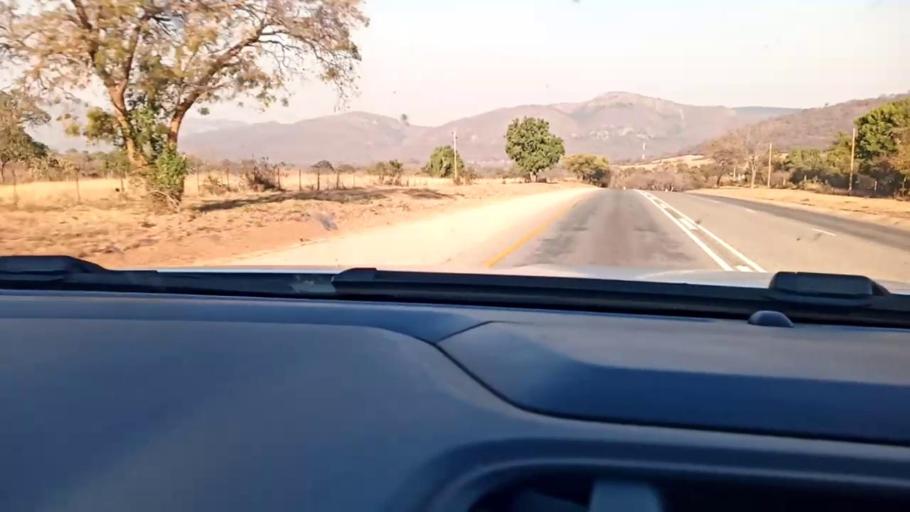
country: ZA
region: Limpopo
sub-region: Mopani District Municipality
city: Duiwelskloof
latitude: -23.6409
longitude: 30.1578
